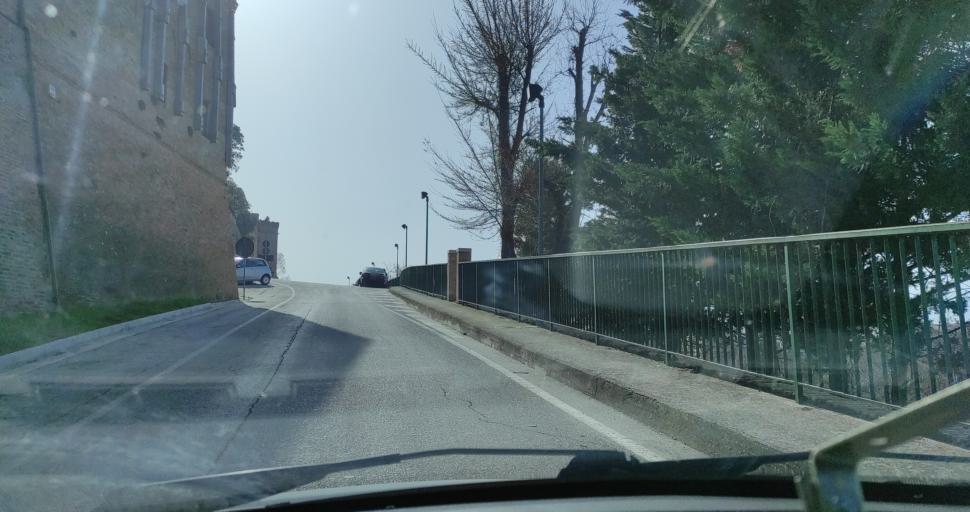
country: IT
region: The Marches
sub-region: Provincia di Macerata
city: Loro Piceno
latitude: 43.1674
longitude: 13.4151
